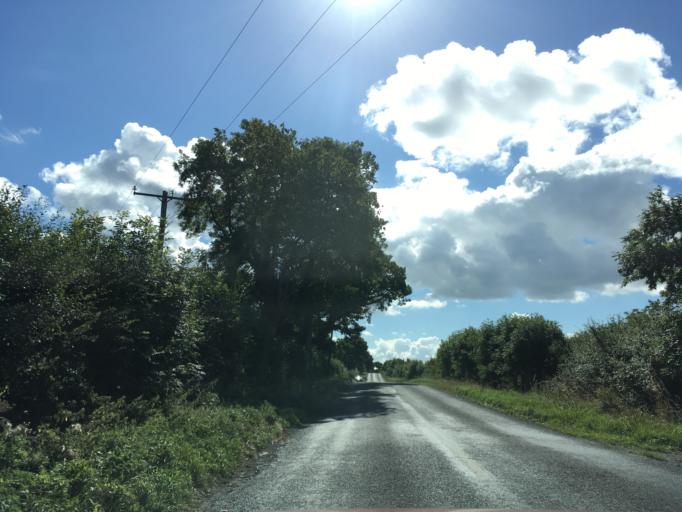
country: IE
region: Munster
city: Cashel
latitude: 52.4491
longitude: -7.9059
